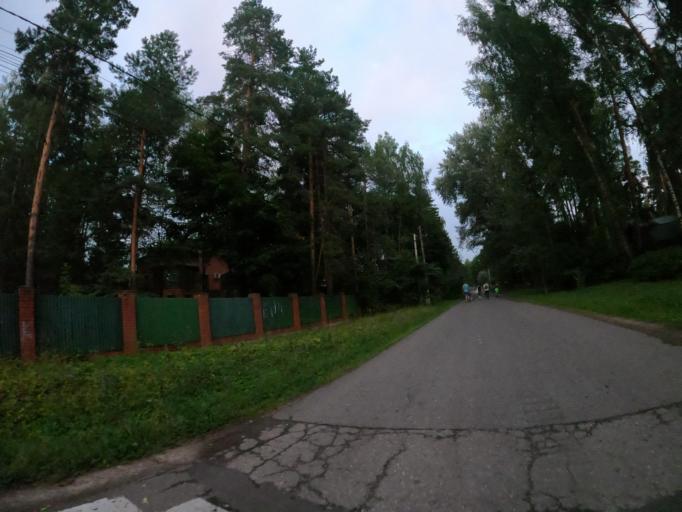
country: RU
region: Moskovskaya
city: Il'inskiy
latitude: 55.6242
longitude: 38.1056
